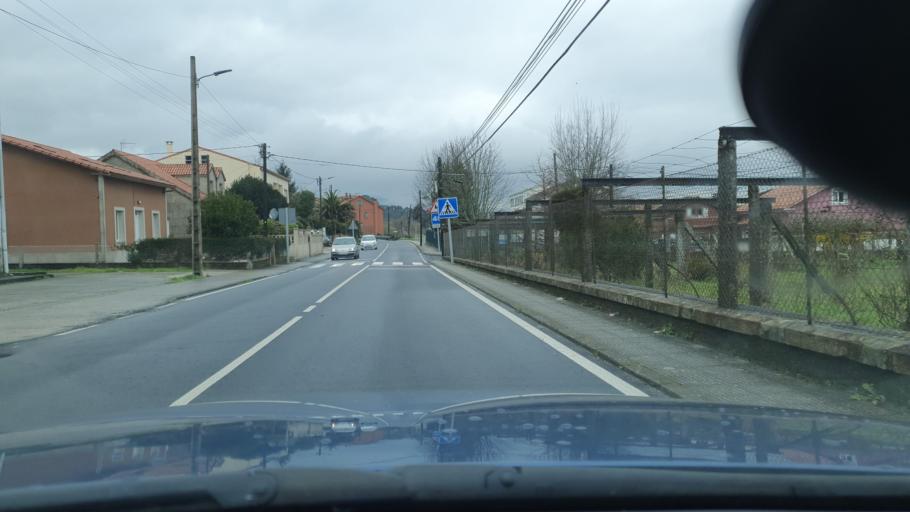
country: ES
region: Galicia
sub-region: Provincia da Coruna
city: Padron
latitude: 42.7486
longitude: -8.6687
